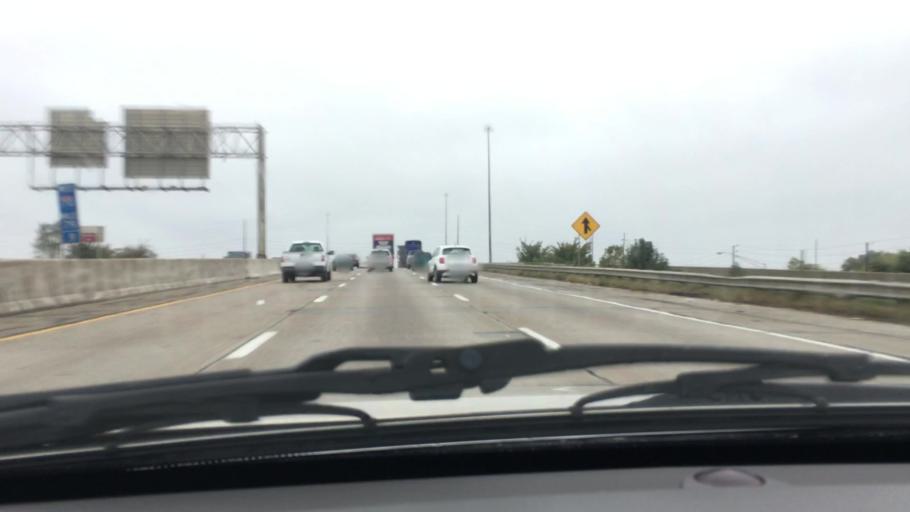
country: US
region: Indiana
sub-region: Marion County
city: Indianapolis
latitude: 39.7537
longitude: -86.1629
